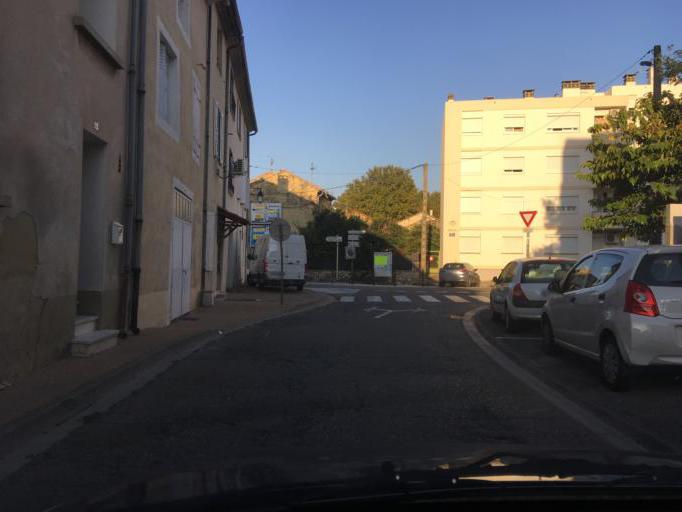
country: FR
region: Languedoc-Roussillon
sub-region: Departement du Gard
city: Roquemaure
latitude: 44.0513
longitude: 4.7808
